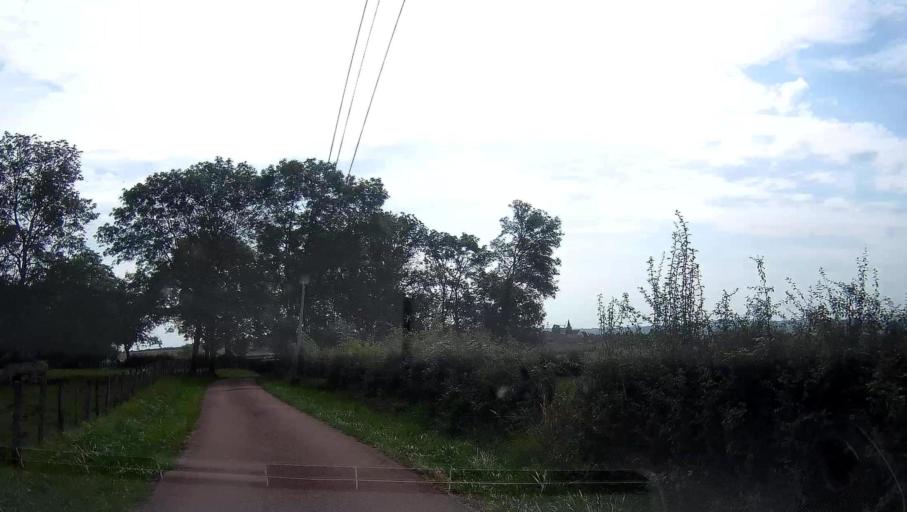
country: FR
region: Bourgogne
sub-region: Departement de Saone-et-Loire
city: Couches
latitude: 46.8971
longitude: 4.6130
